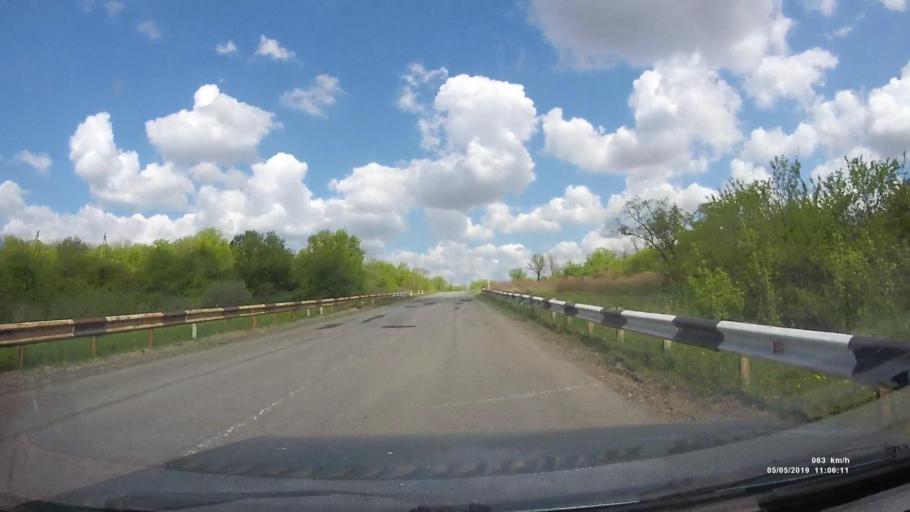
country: RU
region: Rostov
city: Ust'-Donetskiy
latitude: 47.7130
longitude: 40.9111
